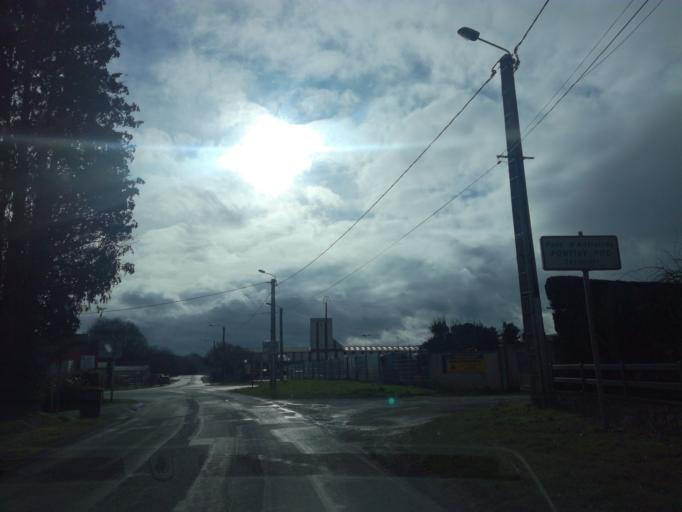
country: FR
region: Brittany
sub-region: Departement du Morbihan
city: Le Sourn
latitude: 48.0377
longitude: -2.9718
